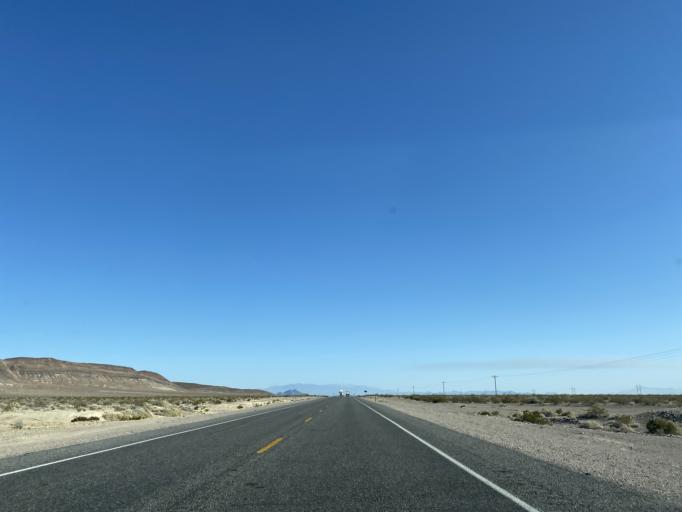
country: US
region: Nevada
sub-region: Nye County
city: Beatty
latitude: 36.6930
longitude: -116.5678
